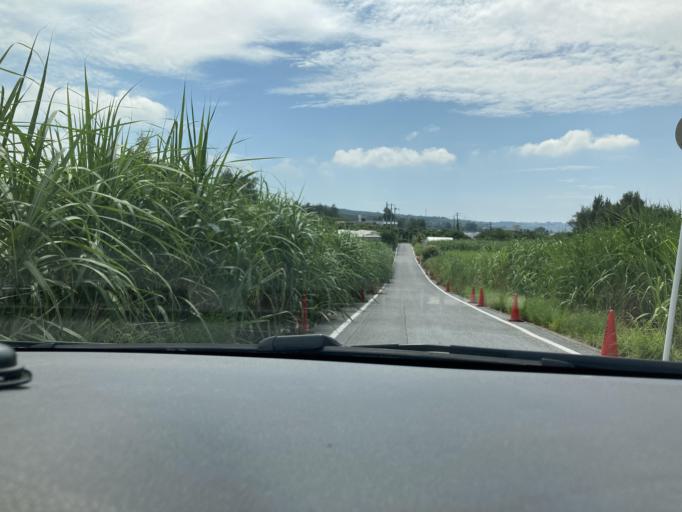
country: JP
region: Okinawa
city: Ishikawa
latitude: 26.4403
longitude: 127.7685
